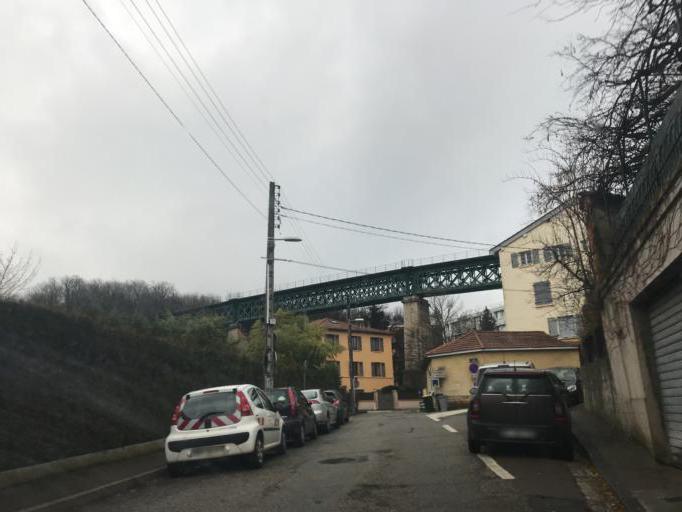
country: FR
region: Rhone-Alpes
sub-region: Departement du Rhone
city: Fontaines-sur-Saone
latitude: 45.8373
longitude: 4.8410
